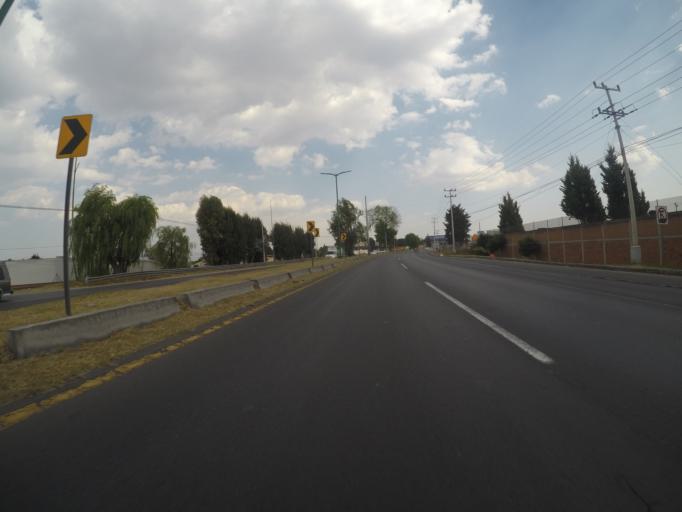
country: MX
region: Morelos
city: San Miguel Totocuitlapilco
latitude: 19.2415
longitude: -99.6007
